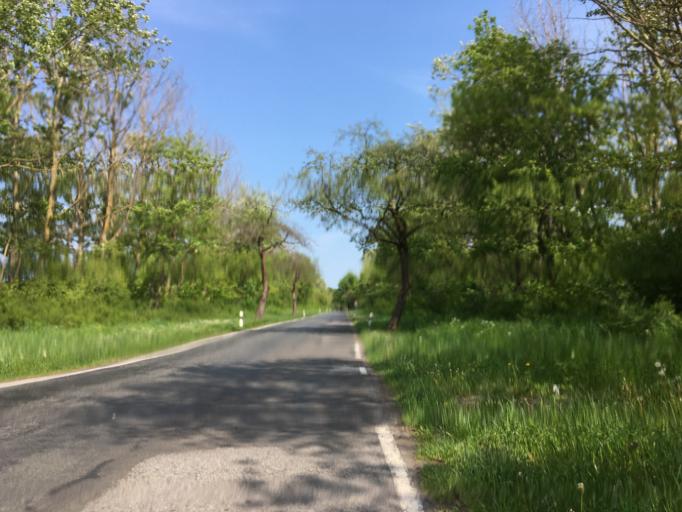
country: DE
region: Brandenburg
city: Werneuchen
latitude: 52.6617
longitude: 13.7314
